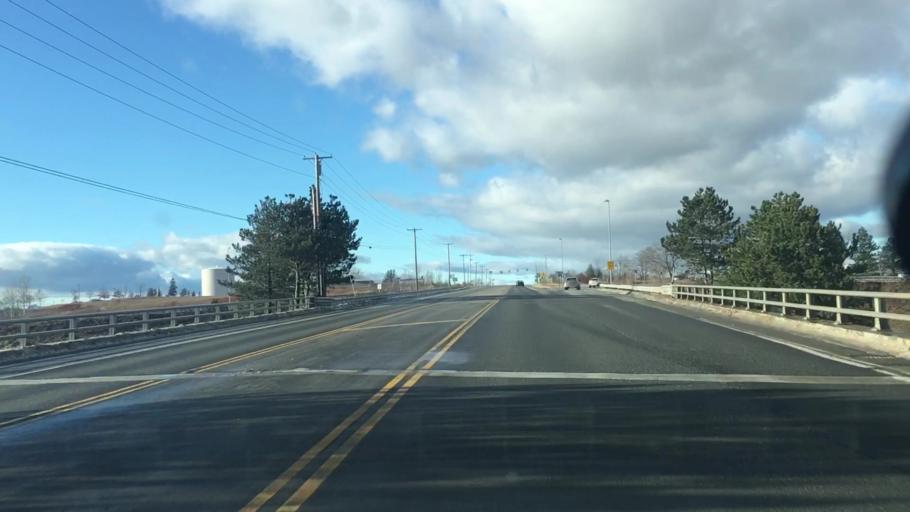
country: US
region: Maine
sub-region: Penobscot County
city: Holden
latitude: 44.7712
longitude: -68.7213
